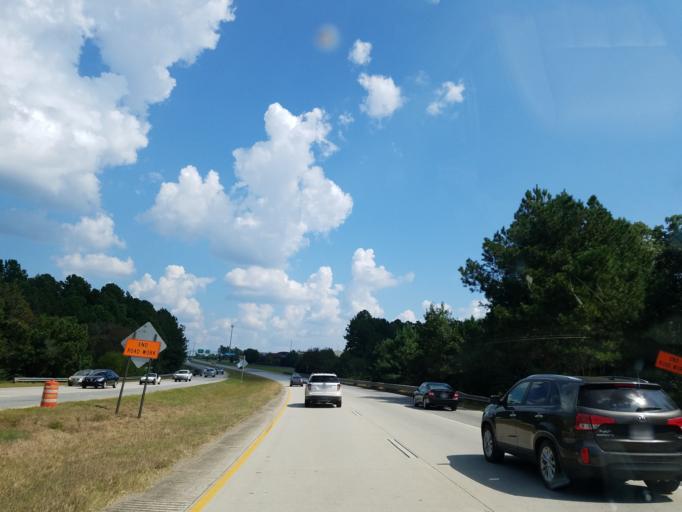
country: US
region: Georgia
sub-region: Oconee County
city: Watkinsville
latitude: 33.9107
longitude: -83.4635
